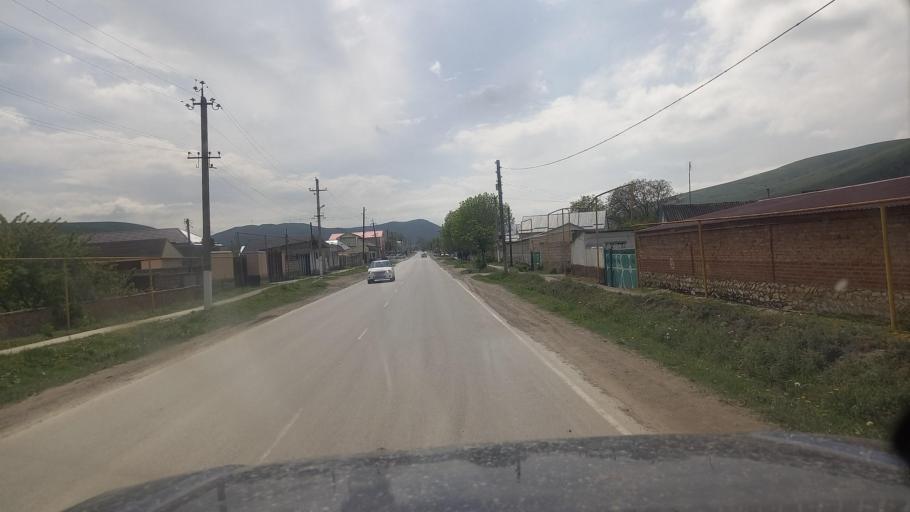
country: RU
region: Kabardino-Balkariya
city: Sarmakovo
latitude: 43.7405
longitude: 43.1888
